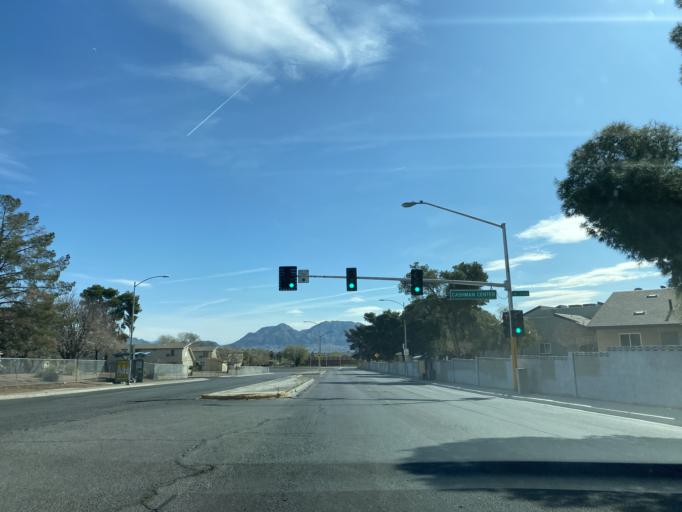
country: US
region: Nevada
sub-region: Clark County
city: Las Vegas
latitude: 36.1782
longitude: -115.1282
